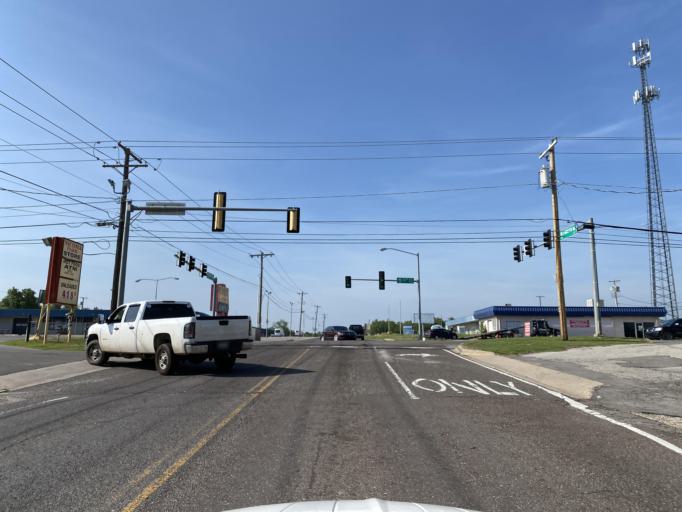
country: US
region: Oklahoma
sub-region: Oklahoma County
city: Nicoma Park
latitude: 35.4927
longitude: -97.3356
